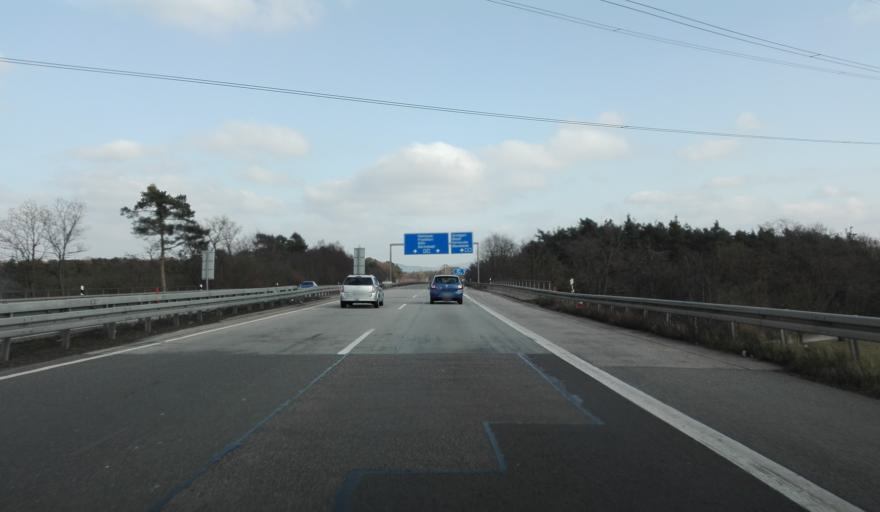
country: DE
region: Hesse
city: Viernheim
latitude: 49.5558
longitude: 8.5408
